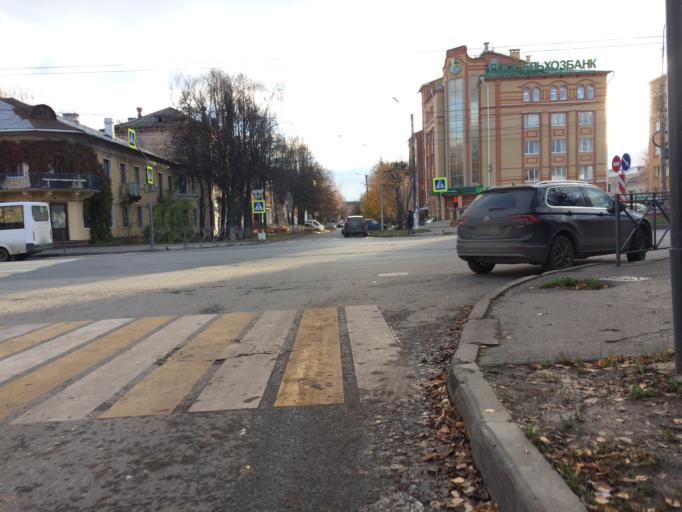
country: RU
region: Mariy-El
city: Yoshkar-Ola
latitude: 56.6402
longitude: 47.8985
